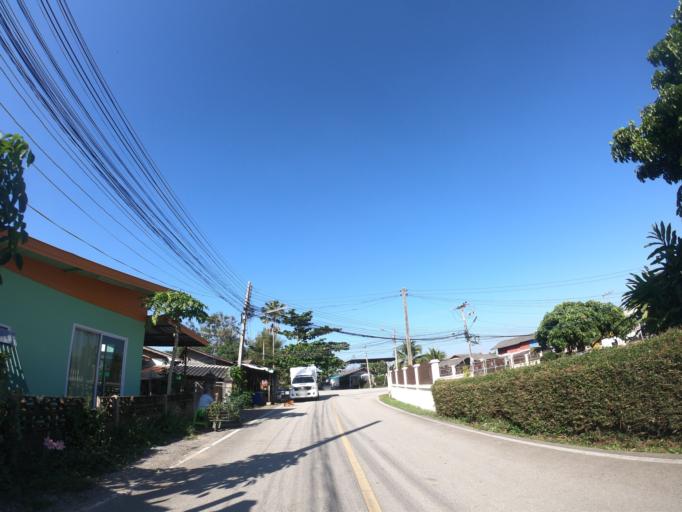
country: TH
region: Chiang Mai
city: Saraphi
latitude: 18.6989
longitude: 98.9932
